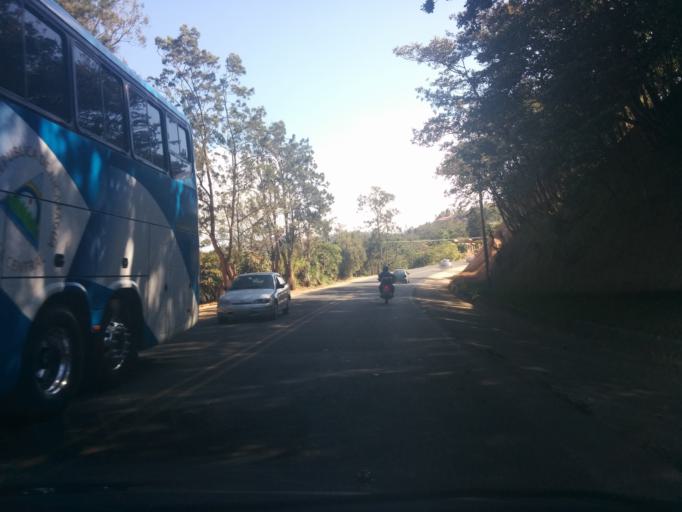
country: CR
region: Alajuela
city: San Rafael
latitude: 10.0537
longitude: -84.5040
